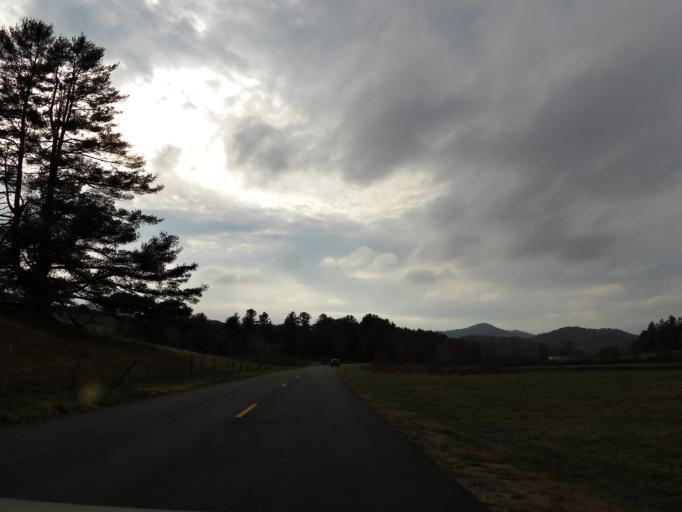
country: US
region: North Carolina
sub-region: Alleghany County
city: Sparta
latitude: 36.3920
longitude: -81.2354
